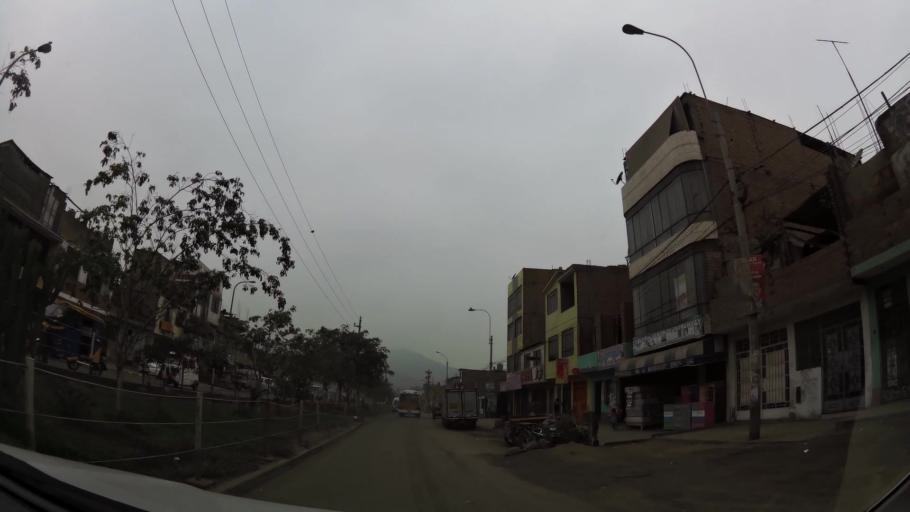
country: PE
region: Lima
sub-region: Lima
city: Independencia
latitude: -11.9452
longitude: -76.9887
